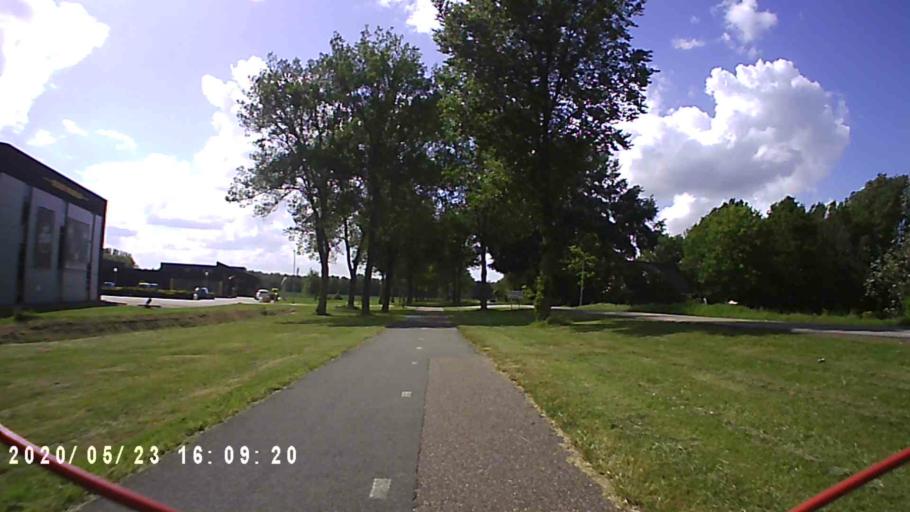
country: NL
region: Groningen
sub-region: Gemeente Appingedam
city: Appingedam
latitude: 53.2476
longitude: 6.8853
